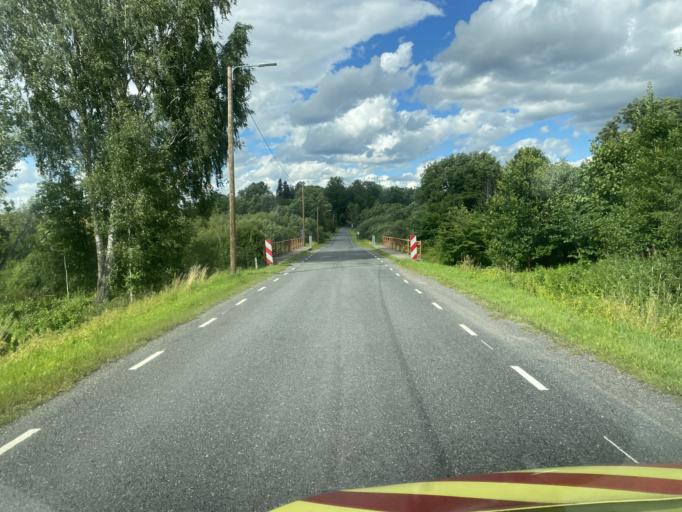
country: EE
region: Viljandimaa
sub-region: Viiratsi vald
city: Viiratsi
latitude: 58.3934
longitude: 25.7625
